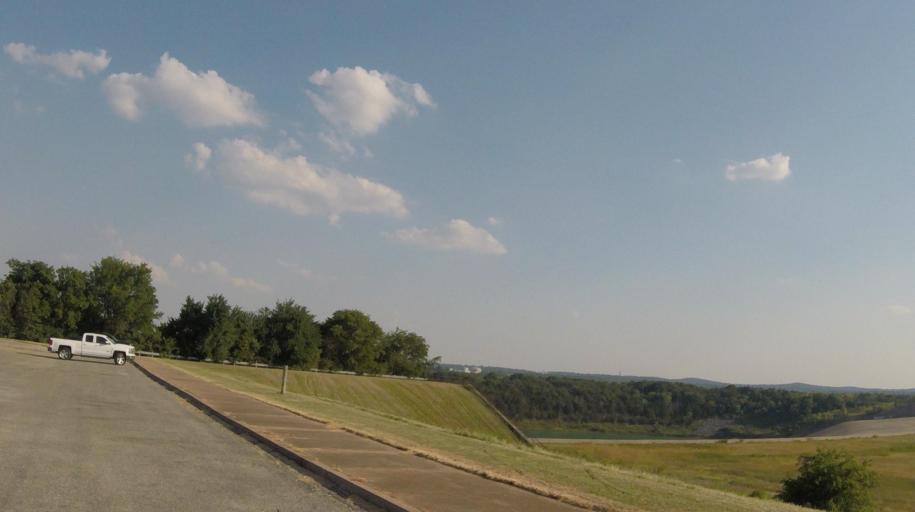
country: US
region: Texas
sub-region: Grayson County
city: Denison
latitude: 33.8156
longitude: -96.5728
